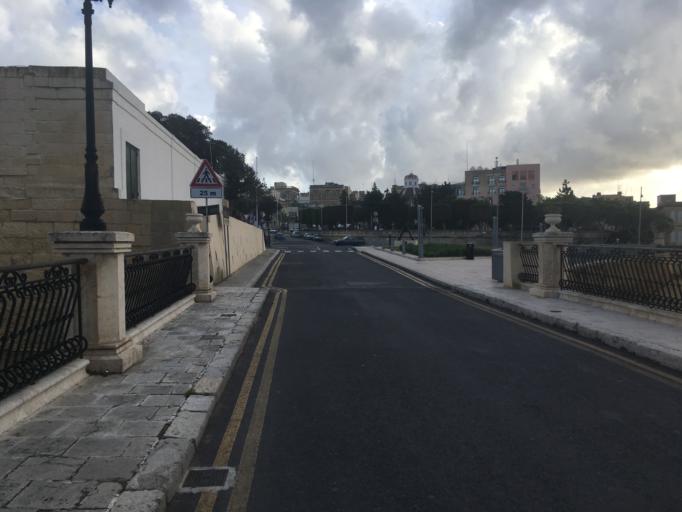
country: MT
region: Bormla
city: Cospicua
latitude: 35.8858
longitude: 14.5230
